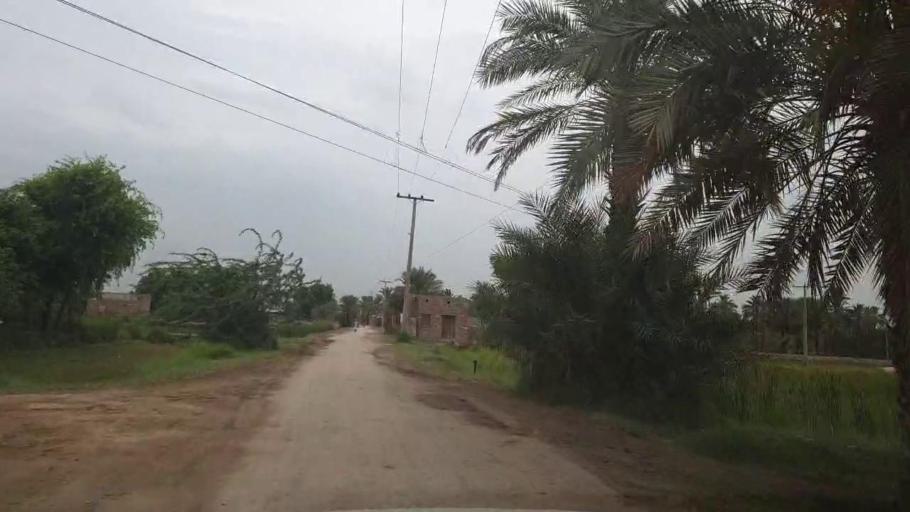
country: PK
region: Sindh
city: Khairpur
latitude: 27.5456
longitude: 68.7396
